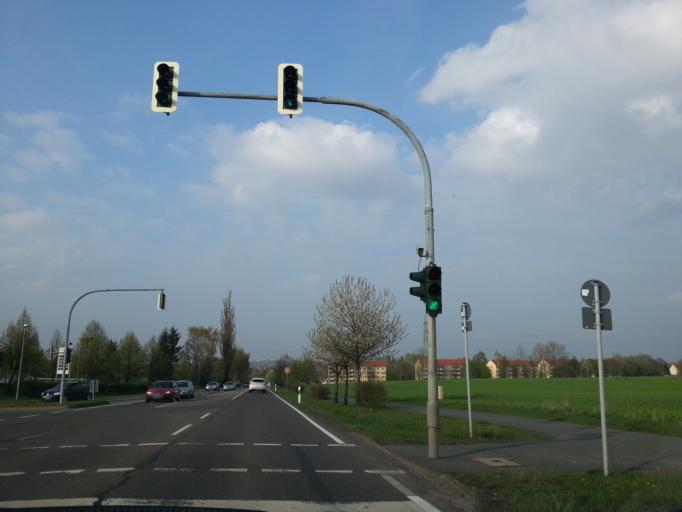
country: DE
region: Saxony
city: Freiberg
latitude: 50.8946
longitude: 13.3327
